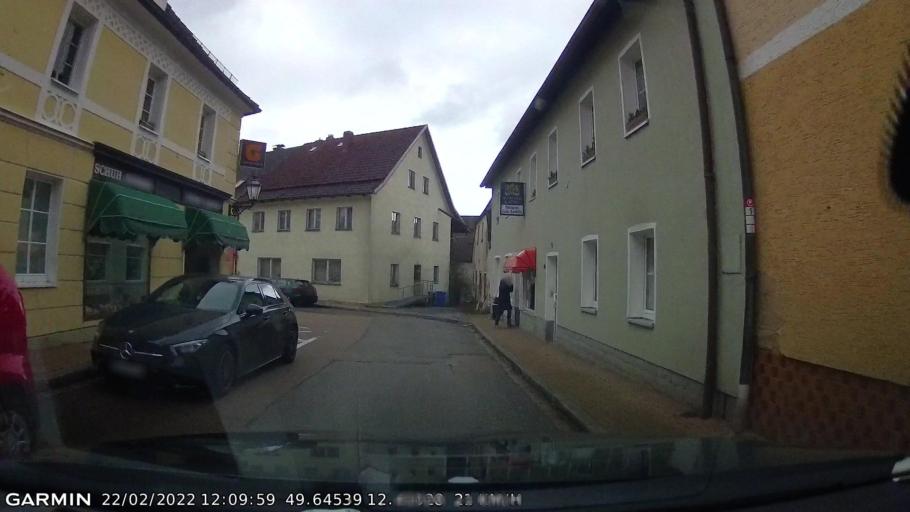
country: DE
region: Bavaria
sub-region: Upper Palatinate
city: Pleystein
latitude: 49.6454
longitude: 12.4102
